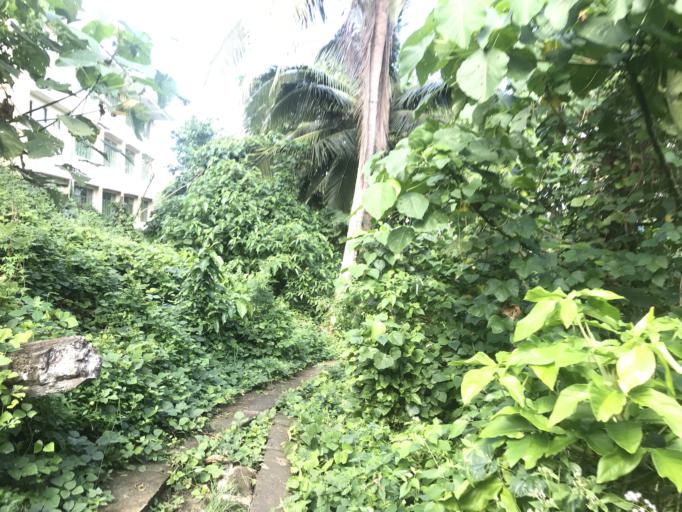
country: PH
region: Calabarzon
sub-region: Province of Quezon
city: Macalelon
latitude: 13.7826
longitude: 122.1406
